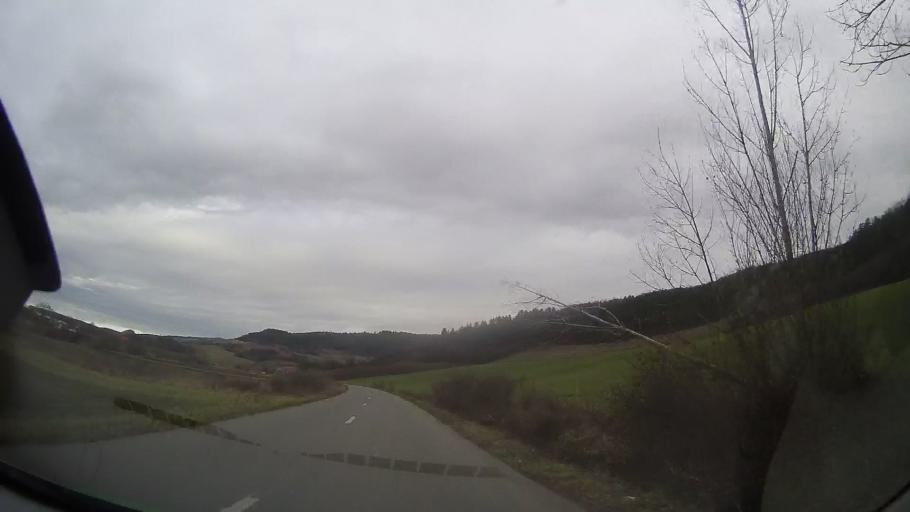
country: RO
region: Mures
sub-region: Comuna Bala
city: Bala
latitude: 46.7295
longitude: 24.5437
